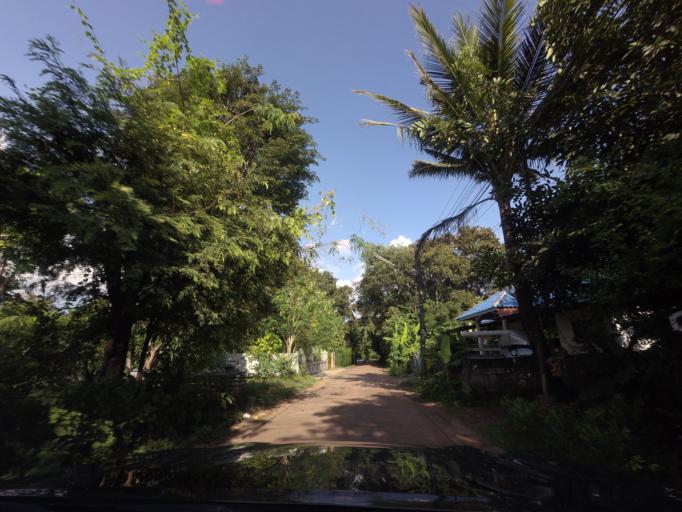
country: TH
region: Nong Khai
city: Nong Khai
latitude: 17.8859
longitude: 102.7718
